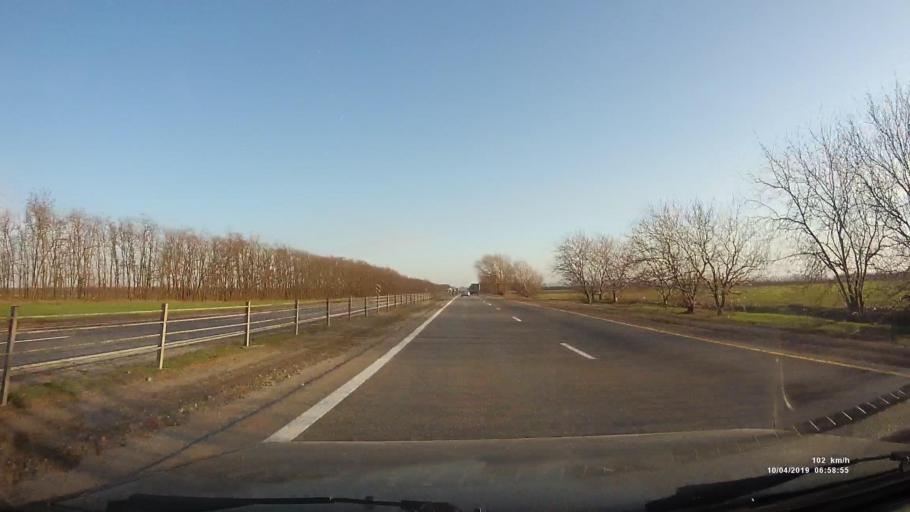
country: RU
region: Rostov
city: Grushevskaya
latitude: 47.5588
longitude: 39.9677
